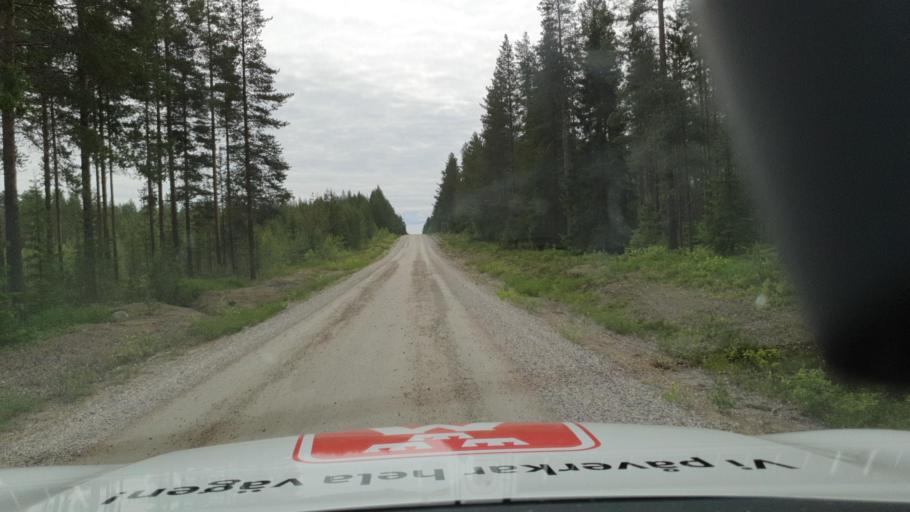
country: SE
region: Vaesterbotten
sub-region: Skelleftea Kommun
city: Forsbacka
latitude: 64.6480
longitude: 20.4500
